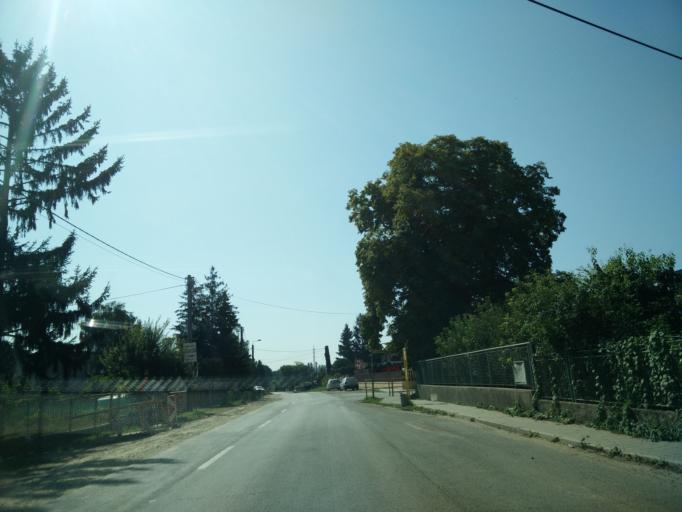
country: SK
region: Nitriansky
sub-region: Okres Nitra
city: Nitra
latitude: 48.3305
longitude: 18.0370
